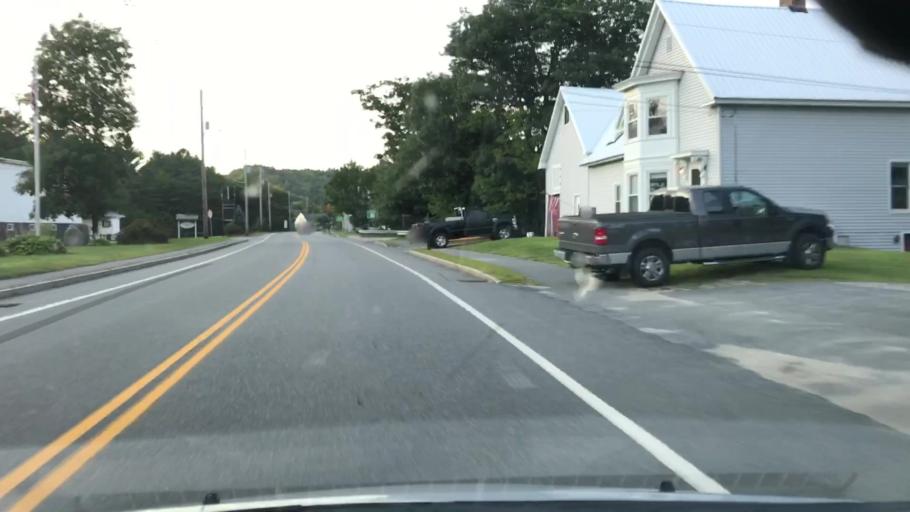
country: US
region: New Hampshire
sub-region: Grafton County
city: Rumney
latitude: 43.9193
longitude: -71.8889
